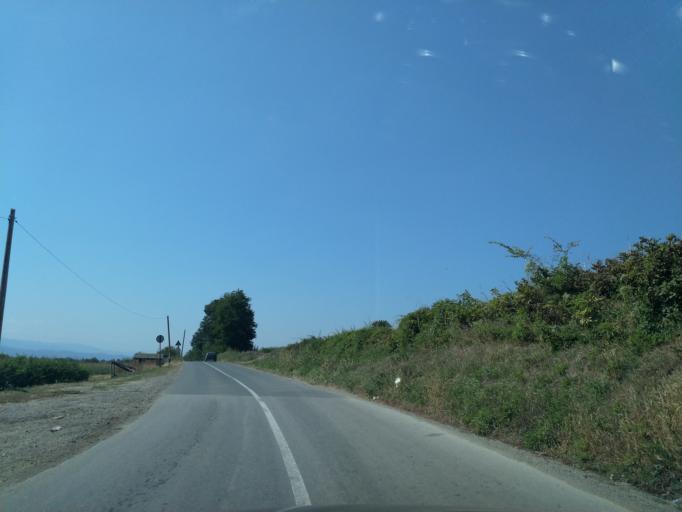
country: RS
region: Central Serbia
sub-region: Rasinski Okrug
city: Krusevac
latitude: 43.6194
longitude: 21.1749
